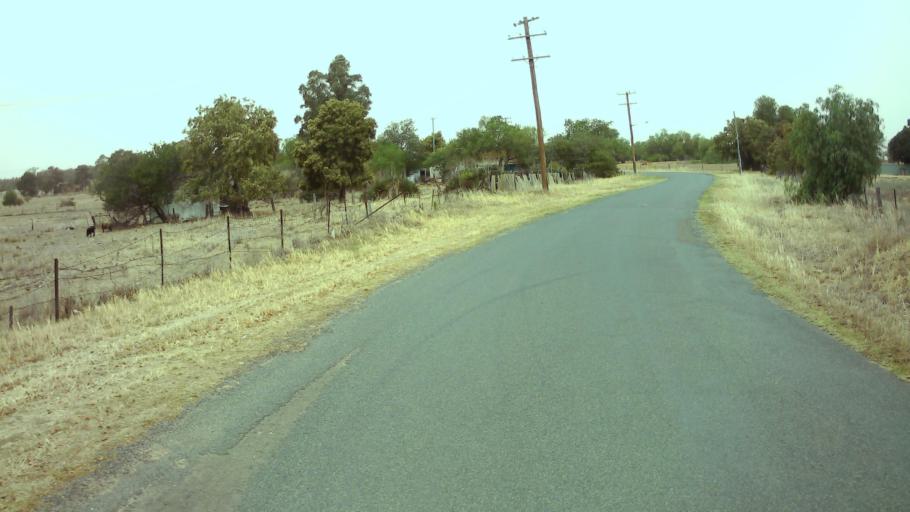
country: AU
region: New South Wales
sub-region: Weddin
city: Grenfell
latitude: -33.8990
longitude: 148.1670
